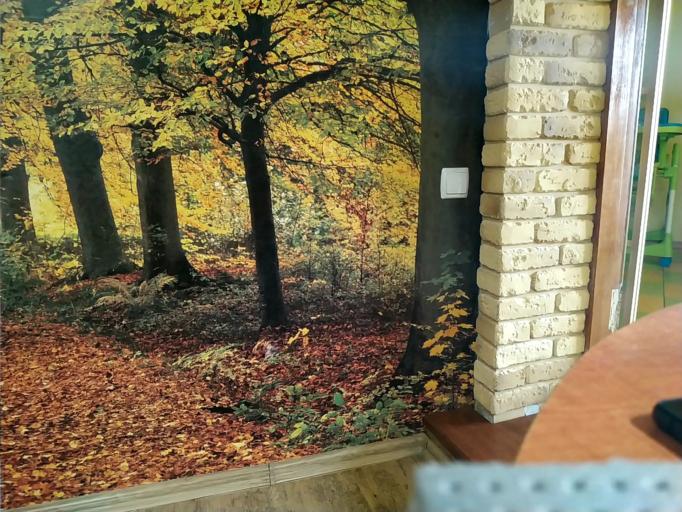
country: RU
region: Jaroslavl
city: Levashevo
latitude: 57.6545
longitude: 40.6264
